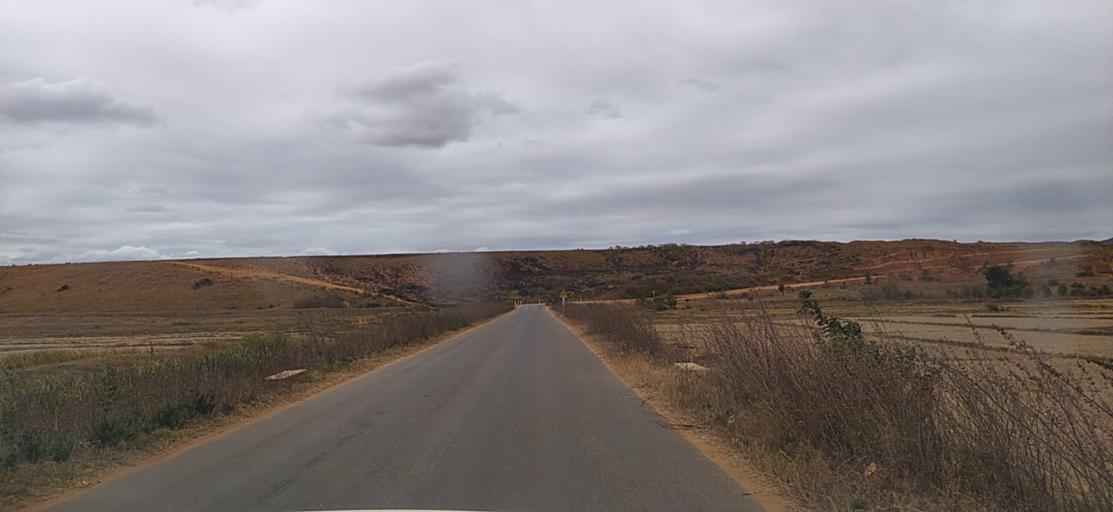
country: MG
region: Alaotra Mangoro
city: Ambatondrazaka
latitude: -17.9136
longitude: 48.2602
